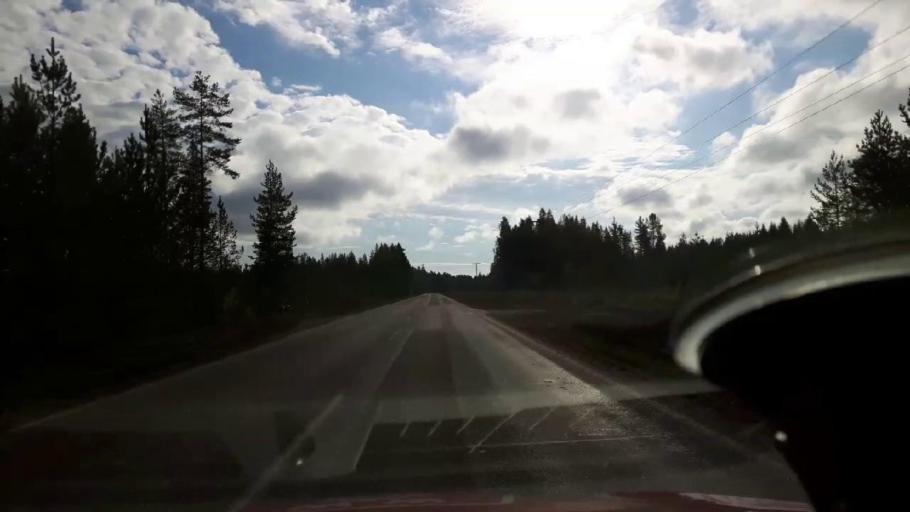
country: SE
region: Jaemtland
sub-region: Harjedalens Kommun
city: Sveg
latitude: 62.1157
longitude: 15.0476
